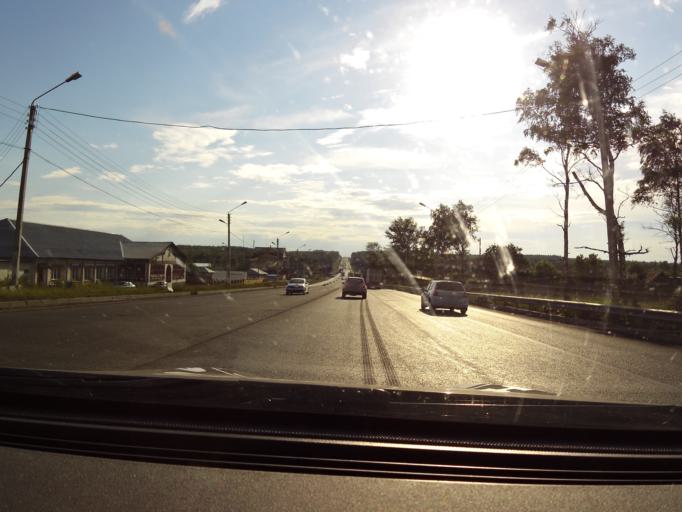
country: RU
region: Vladimir
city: Melekhovo
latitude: 56.2126
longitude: 41.3324
